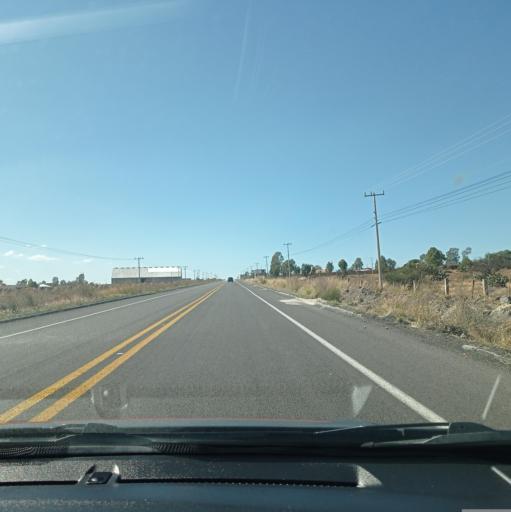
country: MX
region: Jalisco
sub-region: San Julian
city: Colonia Veintitres de Mayo
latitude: 21.0105
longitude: -102.2299
